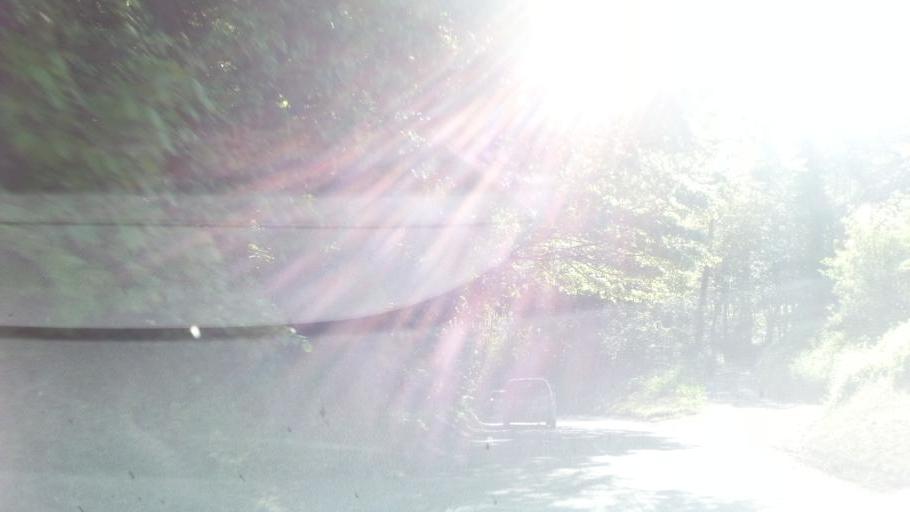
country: GB
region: England
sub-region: Somerset
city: Milborne Port
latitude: 50.9705
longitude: -2.4241
